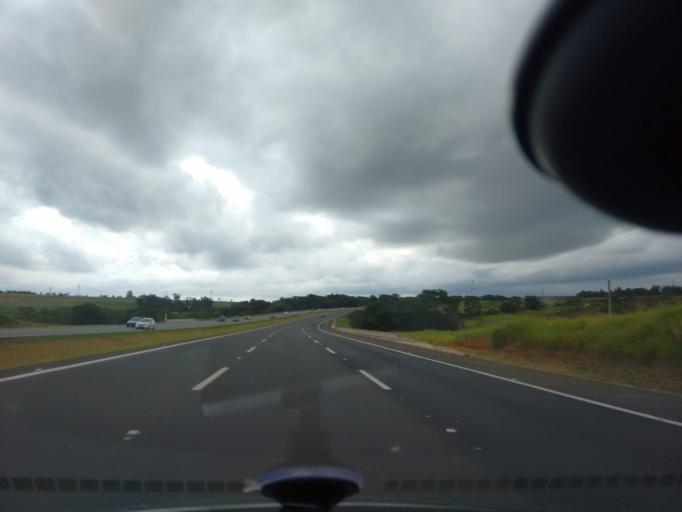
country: BR
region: Sao Paulo
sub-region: Sumare
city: Sumare
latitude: -22.8716
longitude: -47.2695
